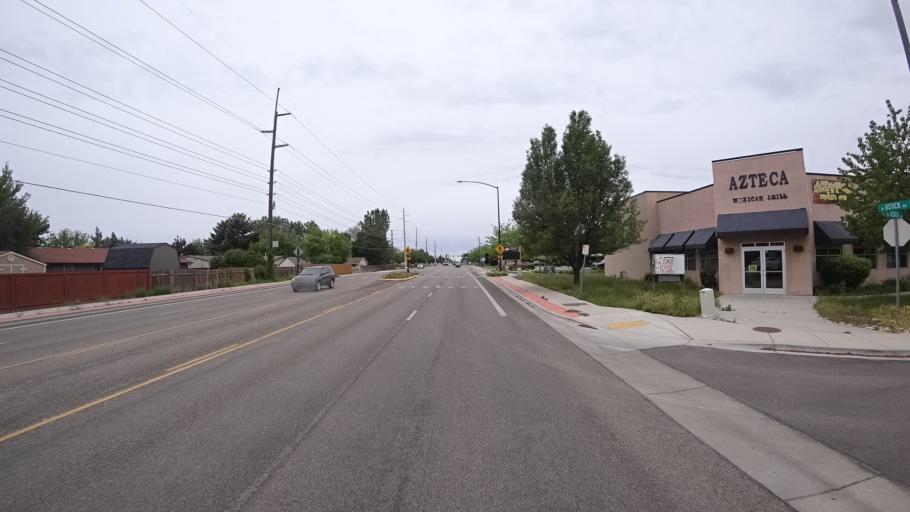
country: US
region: Idaho
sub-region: Ada County
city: Garden City
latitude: 43.6340
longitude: -116.3114
